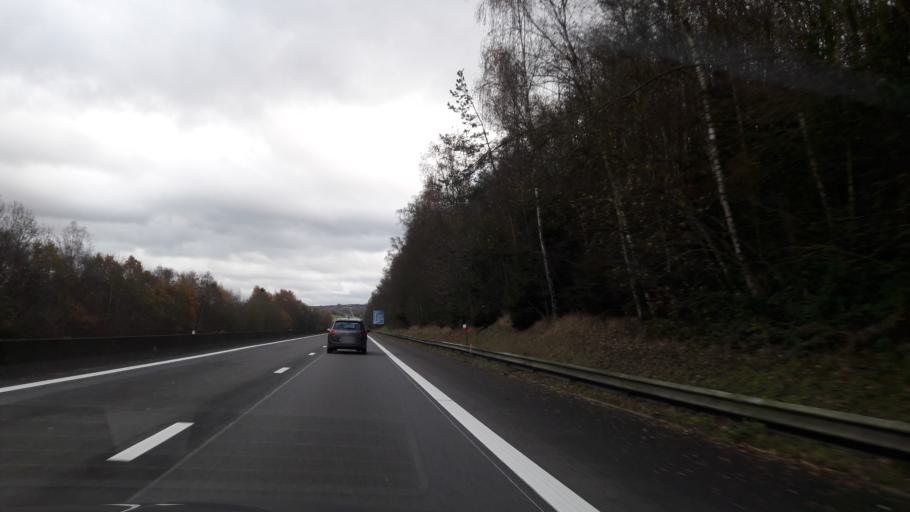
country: BE
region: Wallonia
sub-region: Province de Liege
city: Malmedy
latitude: 50.3784
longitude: 6.0073
